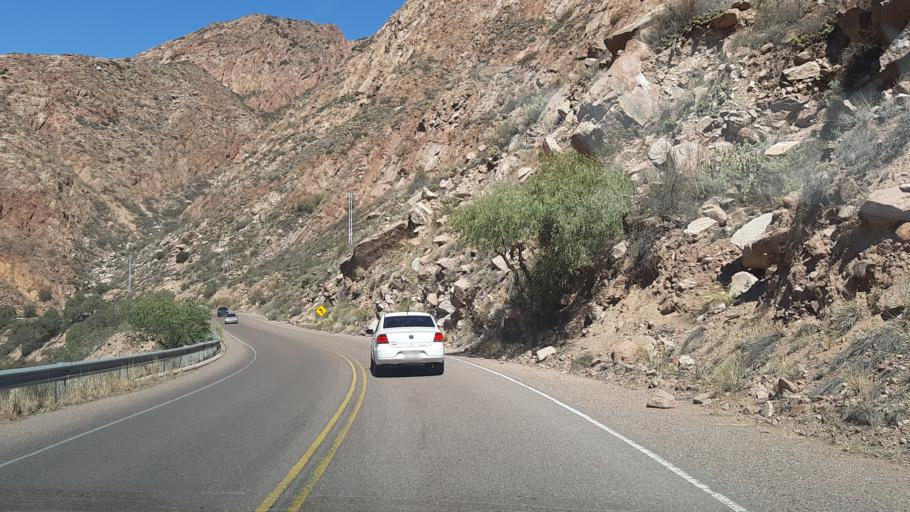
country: AR
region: Mendoza
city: Lujan de Cuyo
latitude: -33.0100
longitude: -69.1234
